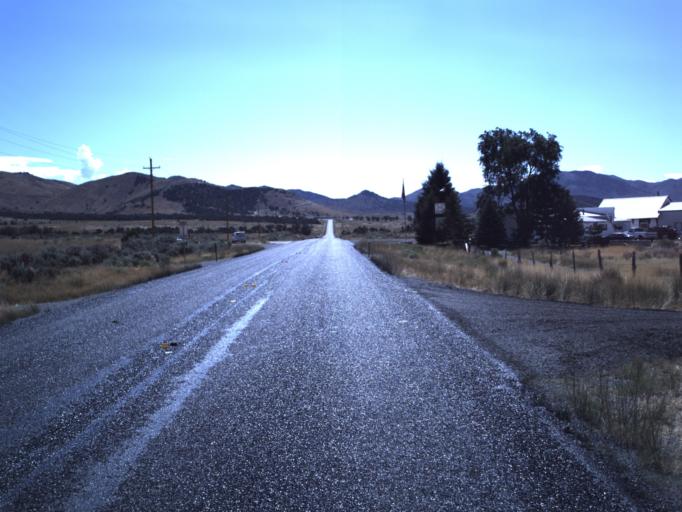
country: US
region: Utah
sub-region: Utah County
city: Genola
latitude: 39.9282
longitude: -112.1625
